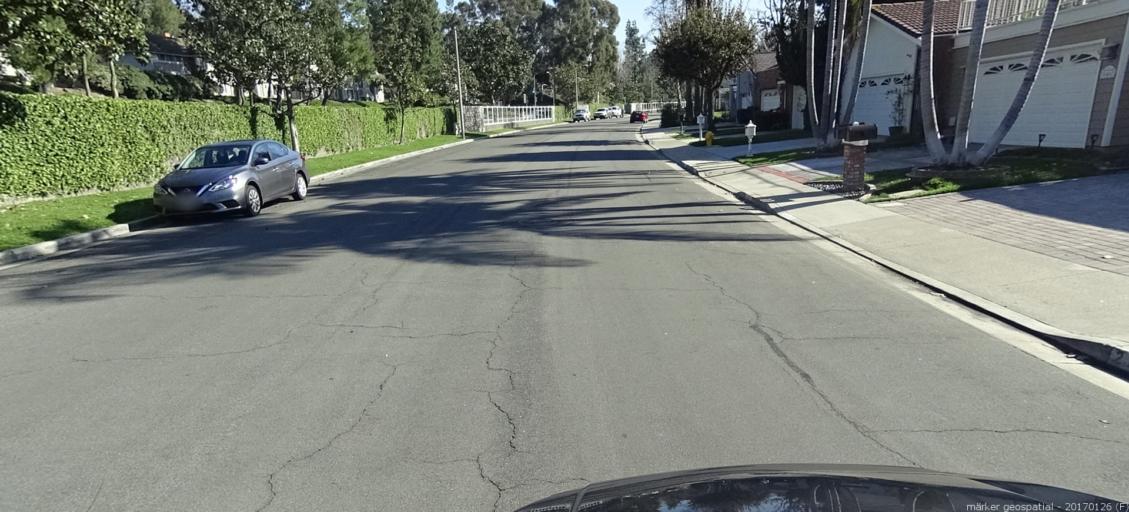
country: US
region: California
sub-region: Orange County
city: Lake Forest
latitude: 33.6483
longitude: -117.7042
